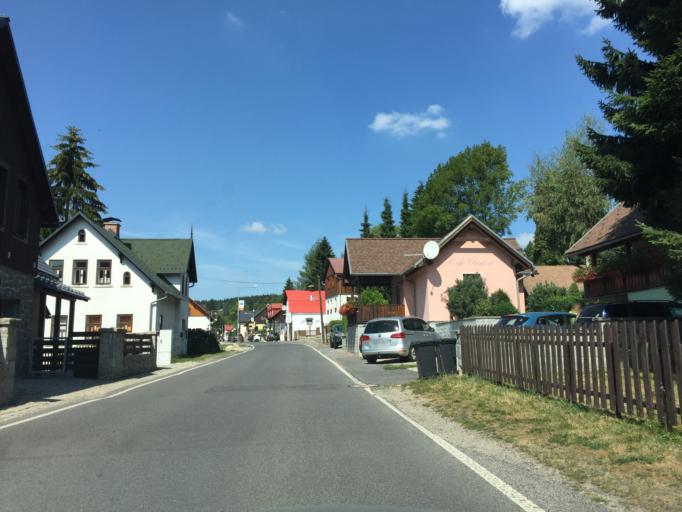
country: CZ
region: Liberecky
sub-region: Okres Jablonec nad Nisou
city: Janov nad Nisou
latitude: 50.7892
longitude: 15.1470
